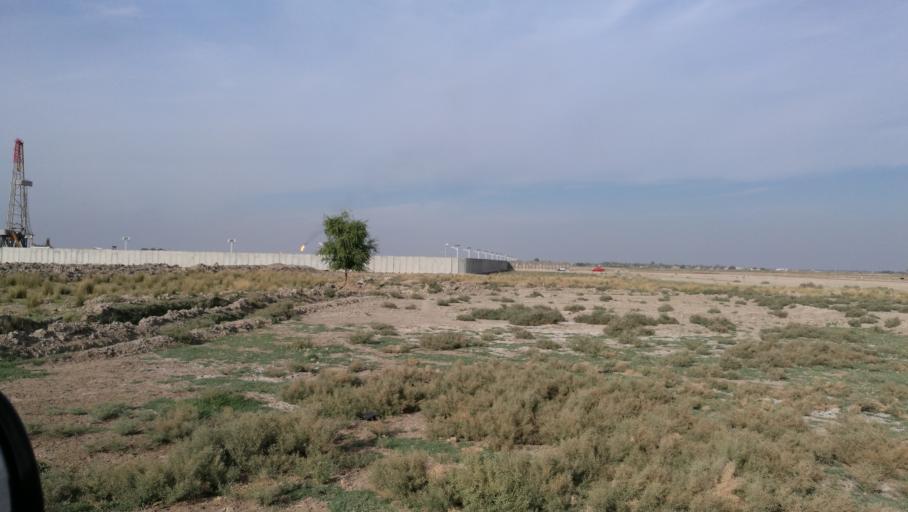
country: IQ
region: Dhi Qar
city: Ar Rifa`i
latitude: 31.7347
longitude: 46.0624
